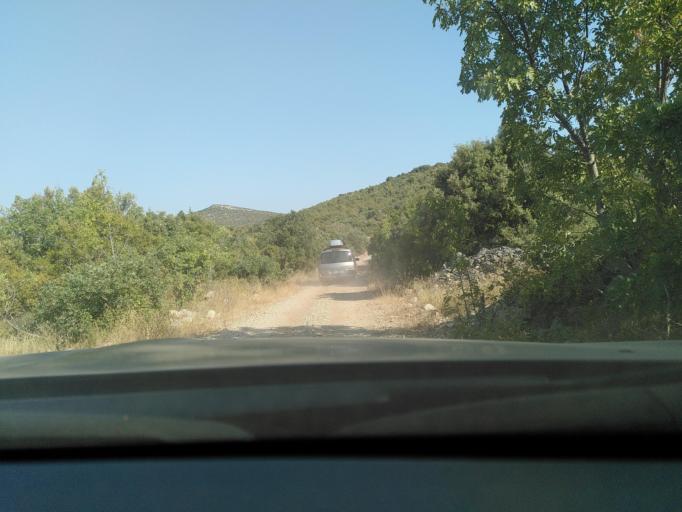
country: HR
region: Splitsko-Dalmatinska
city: Stari Grad
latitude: 43.1608
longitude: 16.5564
